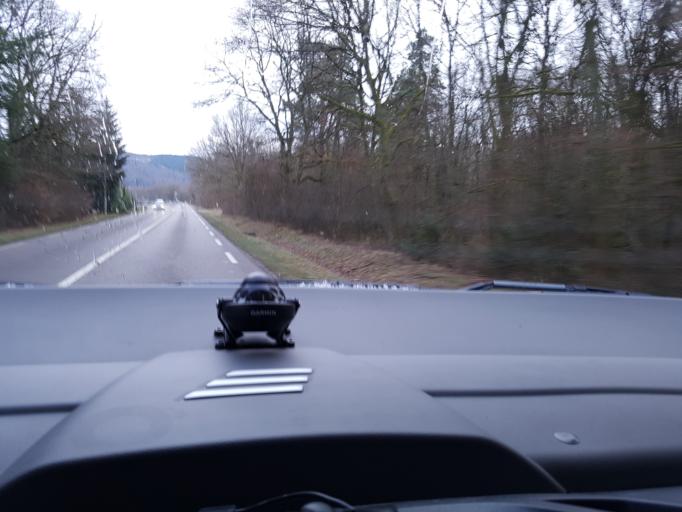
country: FR
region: Alsace
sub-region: Departement du Bas-Rhin
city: Chatenois
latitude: 48.2977
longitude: 7.3569
